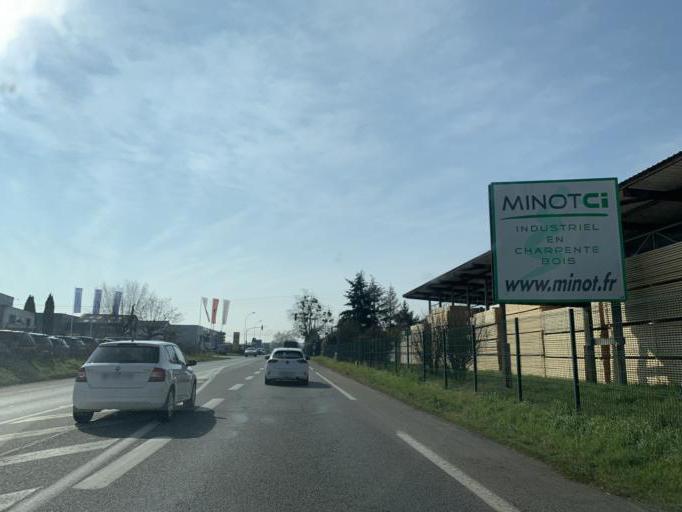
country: FR
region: Rhone-Alpes
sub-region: Departement du Rhone
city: Arnas
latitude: 46.0121
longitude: 4.7252
